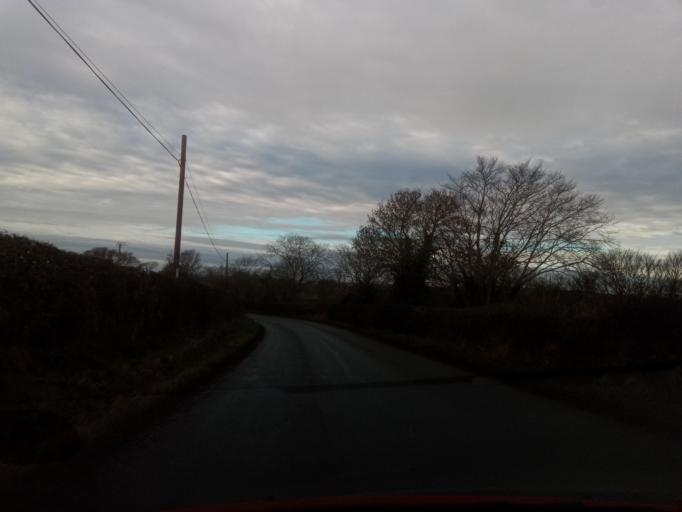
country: GB
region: Scotland
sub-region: The Scottish Borders
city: Coldstream
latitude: 55.7185
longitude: -2.2508
